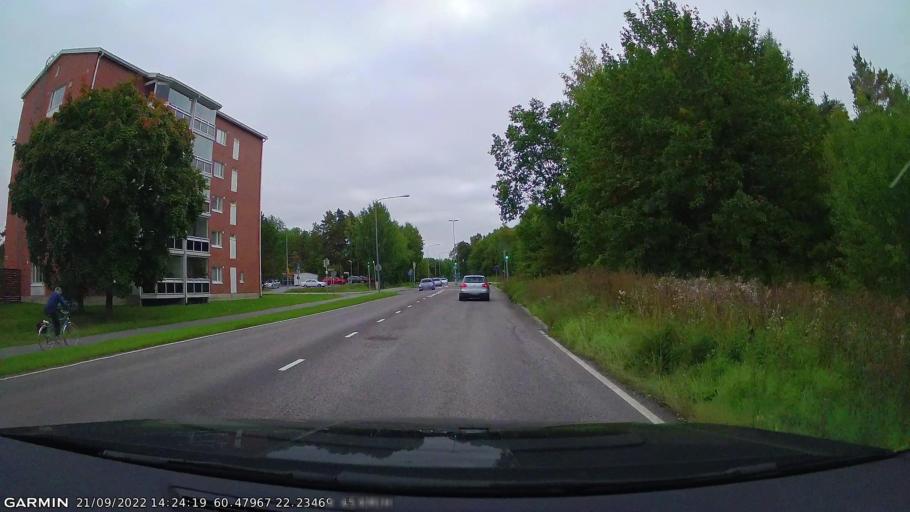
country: FI
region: Varsinais-Suomi
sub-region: Turku
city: Turku
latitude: 60.4795
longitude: 22.2347
